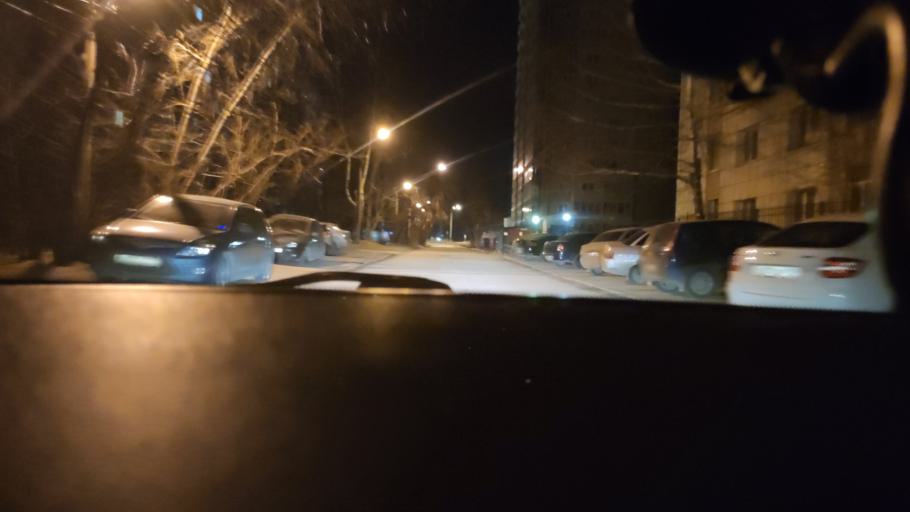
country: RU
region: Perm
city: Kondratovo
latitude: 58.0375
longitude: 56.0378
